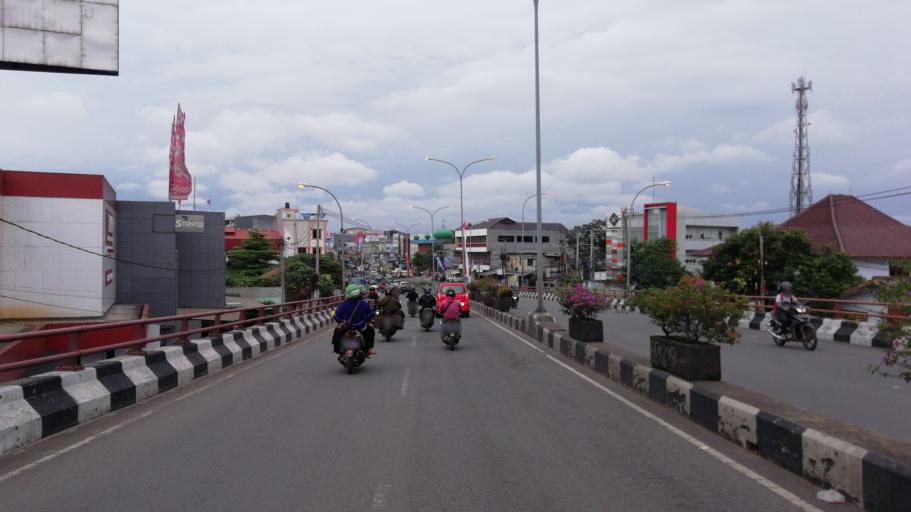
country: ID
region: West Java
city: Depok
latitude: -6.3896
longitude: 106.8202
